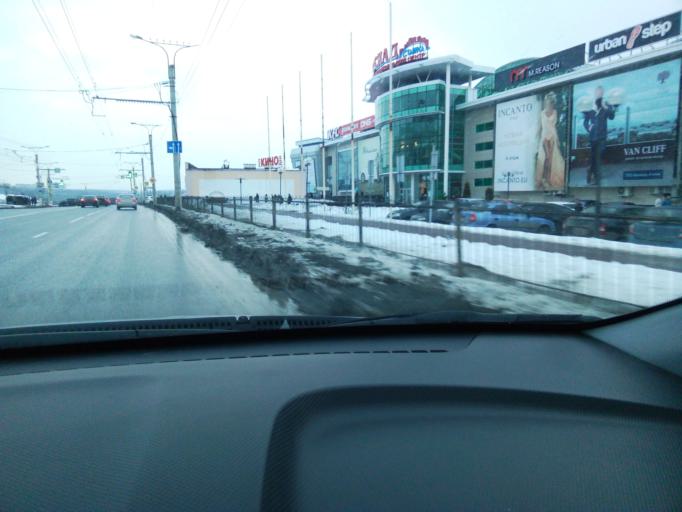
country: RU
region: Chuvashia
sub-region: Cheboksarskiy Rayon
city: Cheboksary
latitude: 56.1358
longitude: 47.2419
